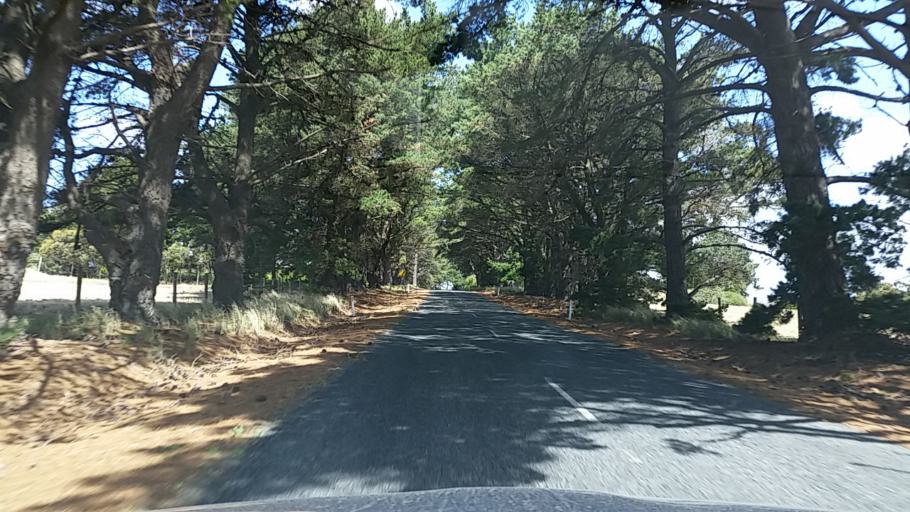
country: AU
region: South Australia
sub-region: Alexandrina
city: Mount Compass
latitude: -35.4442
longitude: 138.6276
